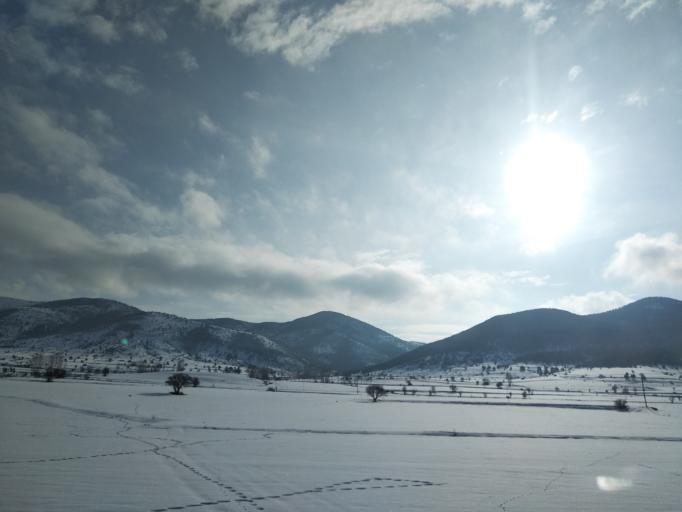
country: TR
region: Gumushane
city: Kelkit
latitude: 39.9952
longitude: 39.5481
